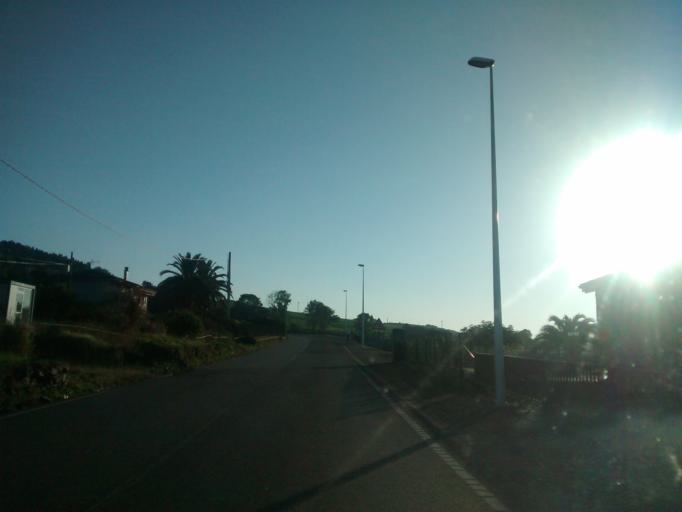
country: ES
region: Cantabria
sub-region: Provincia de Cantabria
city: San Miguel de Meruelo
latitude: 43.4490
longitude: -3.5731
